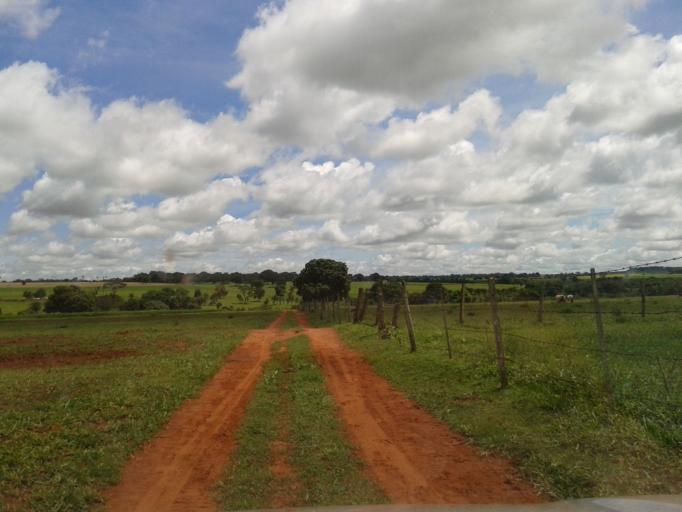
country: BR
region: Minas Gerais
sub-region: Santa Vitoria
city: Santa Vitoria
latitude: -18.7913
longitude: -49.8557
